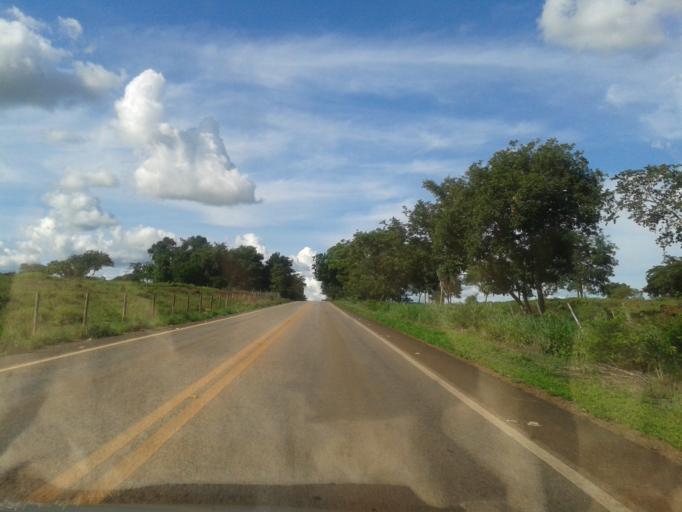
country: BR
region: Goias
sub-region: Mozarlandia
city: Mozarlandia
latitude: -14.6446
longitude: -50.5200
